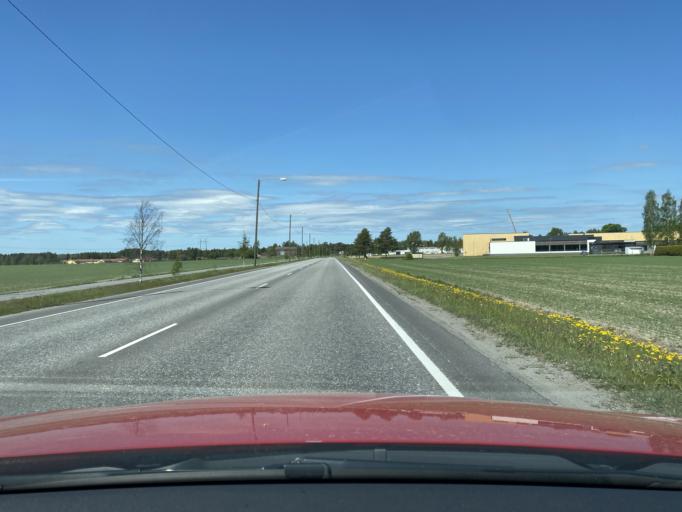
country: FI
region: Satakunta
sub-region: Rauma
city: Eura
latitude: 61.1202
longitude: 22.1382
